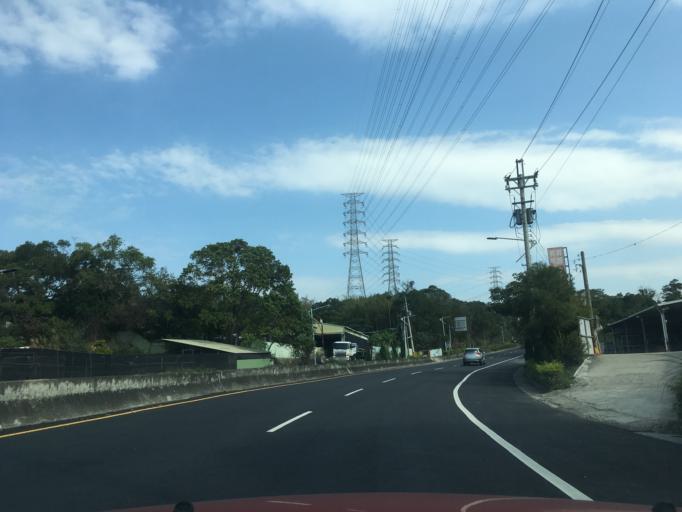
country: TW
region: Taiwan
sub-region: Hsinchu
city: Hsinchu
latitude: 24.7602
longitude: 121.0058
